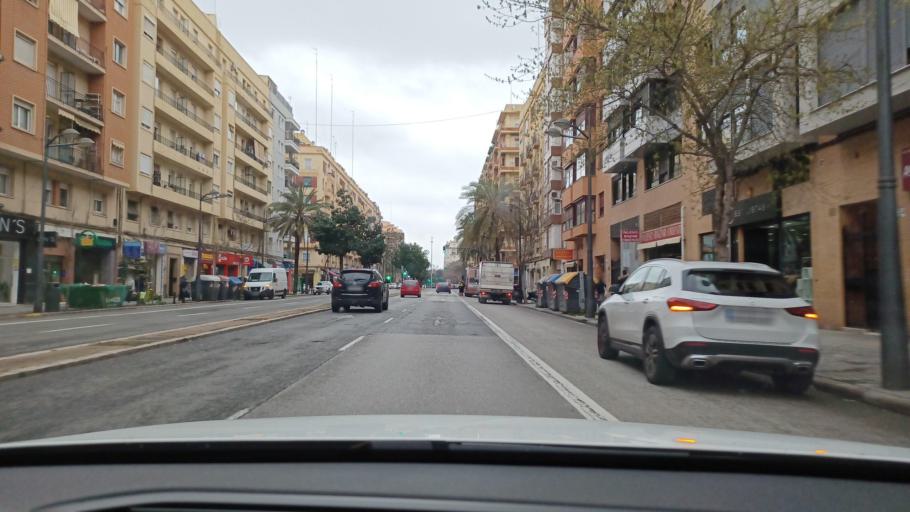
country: ES
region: Valencia
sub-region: Provincia de Valencia
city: Valencia
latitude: 39.4731
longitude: -0.3535
